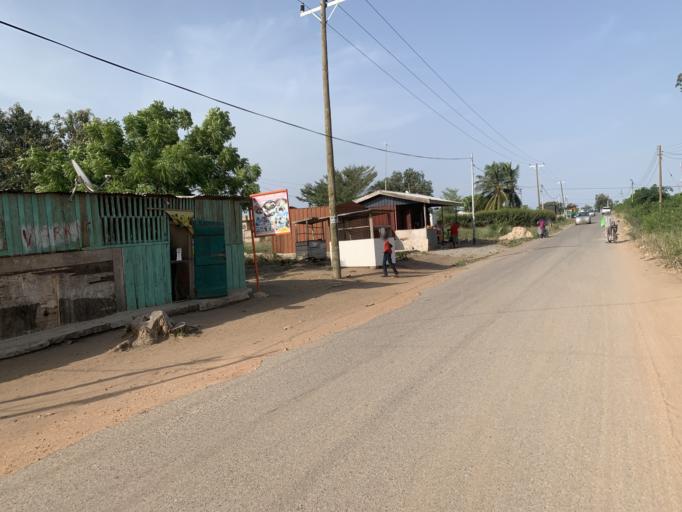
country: GH
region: Central
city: Winneba
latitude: 5.3679
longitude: -0.6470
